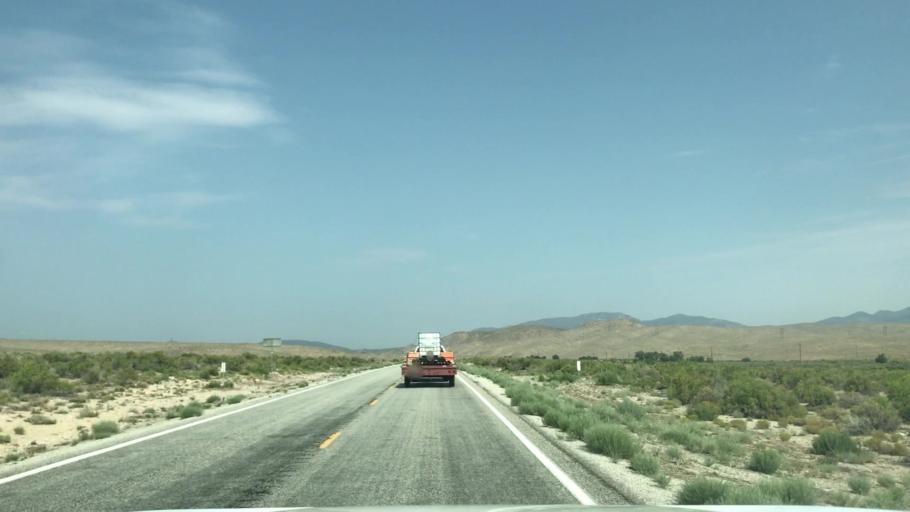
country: US
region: Nevada
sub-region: White Pine County
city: McGill
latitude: 39.0788
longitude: -114.1894
